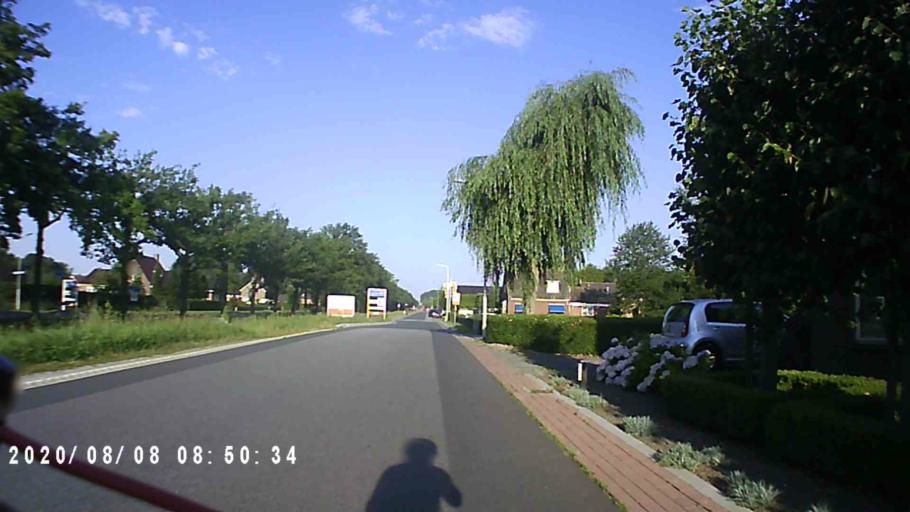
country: NL
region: Groningen
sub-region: Gemeente Leek
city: Leek
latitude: 53.0657
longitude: 6.3266
